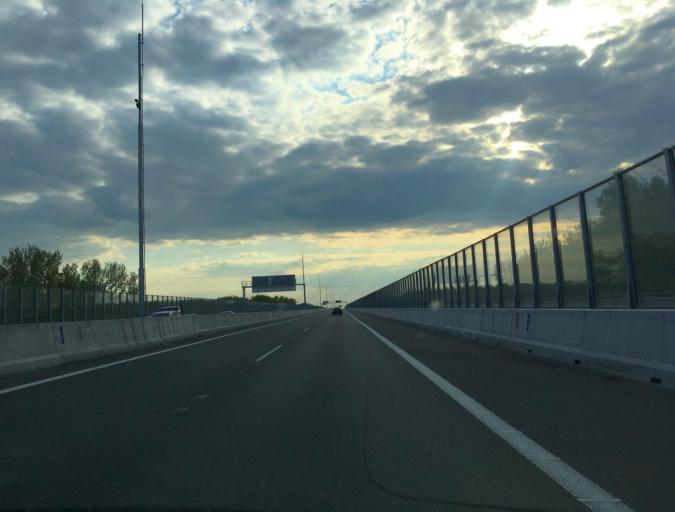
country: SK
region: Bratislavsky
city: Bratislava
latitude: 48.0859
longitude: 17.1612
